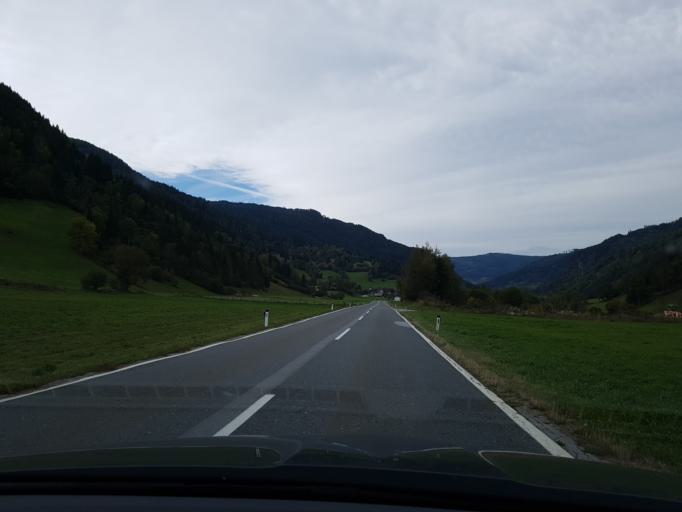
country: AT
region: Salzburg
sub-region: Politischer Bezirk Tamsweg
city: Ramingstein
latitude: 47.0662
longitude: 13.8942
